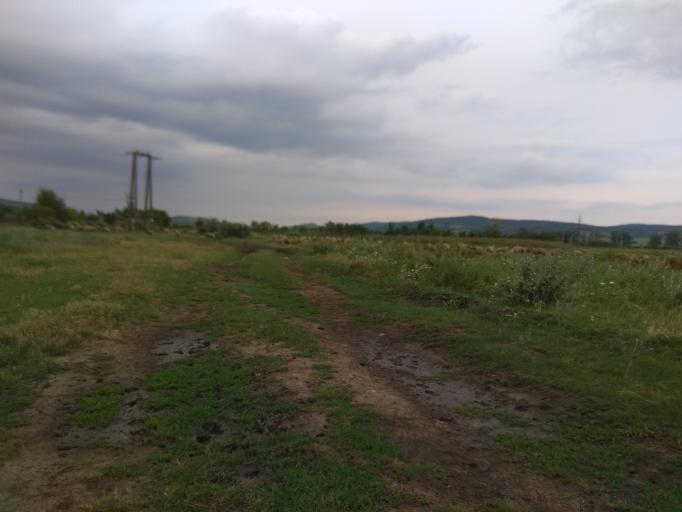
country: HU
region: Borsod-Abauj-Zemplen
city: Bekecs
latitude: 48.1547
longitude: 21.1261
